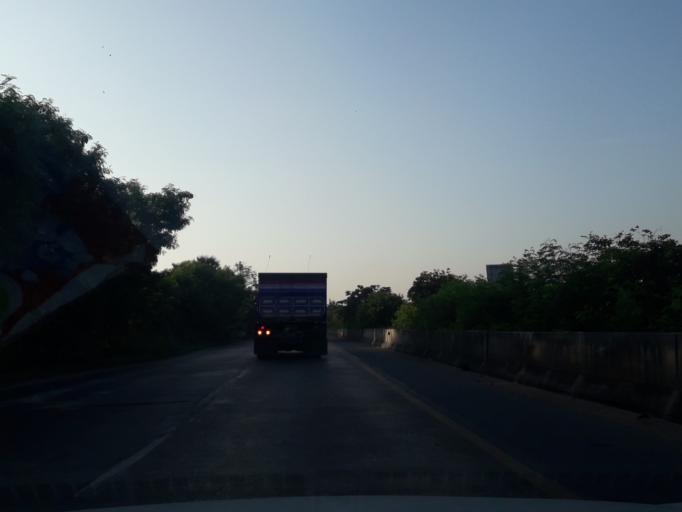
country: TH
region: Phra Nakhon Si Ayutthaya
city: Bang Pa-in
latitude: 14.1840
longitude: 100.5568
